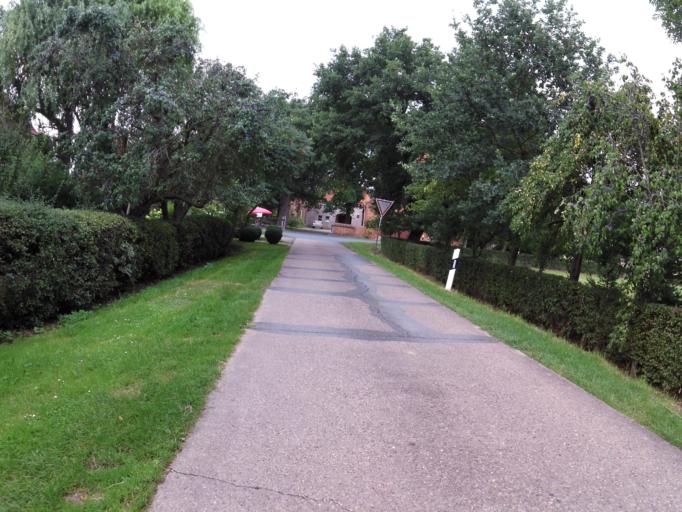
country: DE
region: Lower Saxony
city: Blender
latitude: 52.9139
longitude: 9.1598
